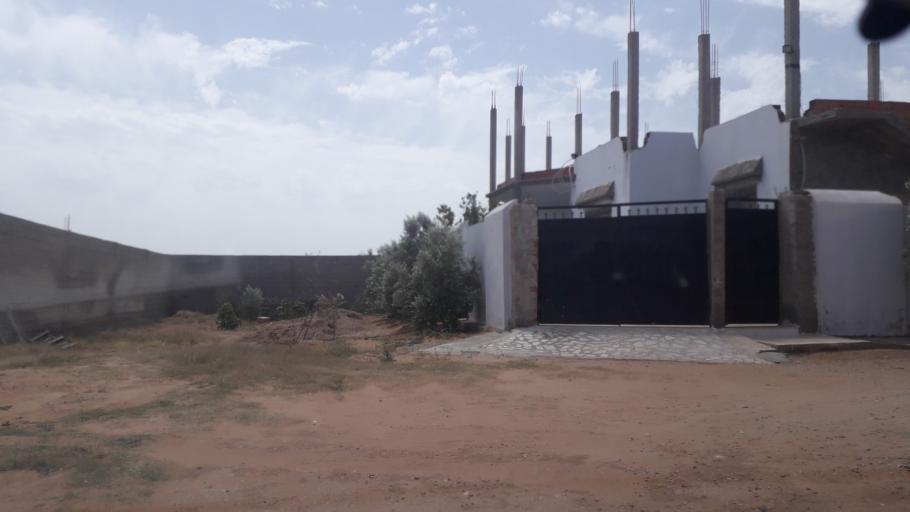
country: TN
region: Safaqis
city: Al Qarmadah
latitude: 34.8357
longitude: 10.7706
